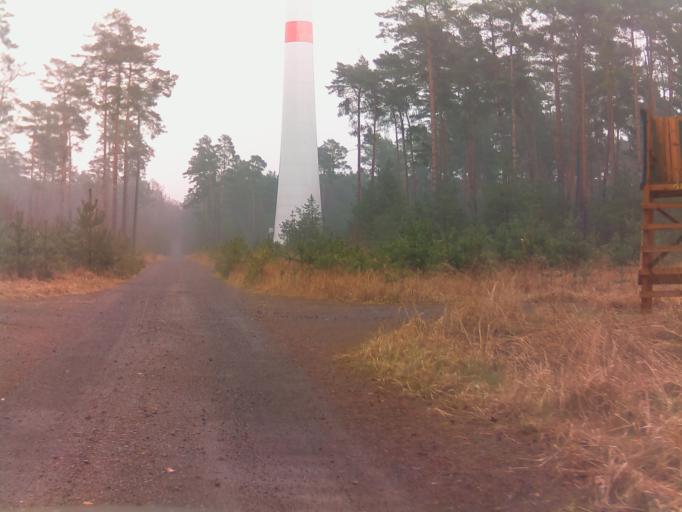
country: DE
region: Brandenburg
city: Jamlitz
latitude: 52.0574
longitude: 14.3637
